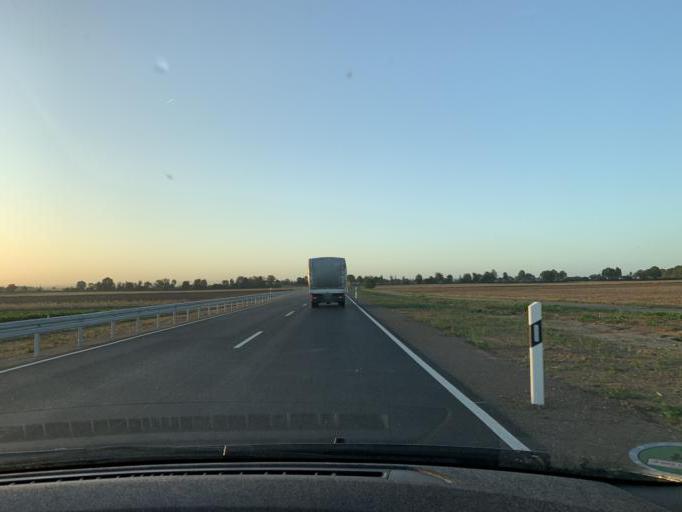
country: DE
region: North Rhine-Westphalia
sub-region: Regierungsbezirk Koln
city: Vettweiss
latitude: 50.7228
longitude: 6.5748
